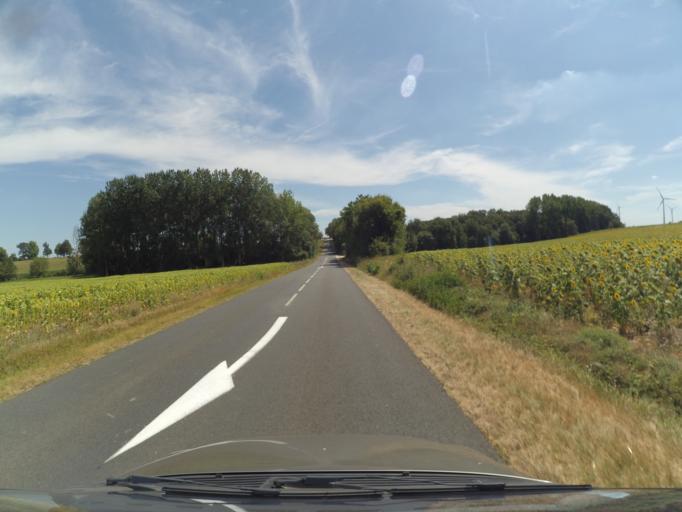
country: FR
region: Poitou-Charentes
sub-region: Departement de la Vienne
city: Saint-Maurice-la-Clouere
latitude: 46.3364
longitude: 0.4637
